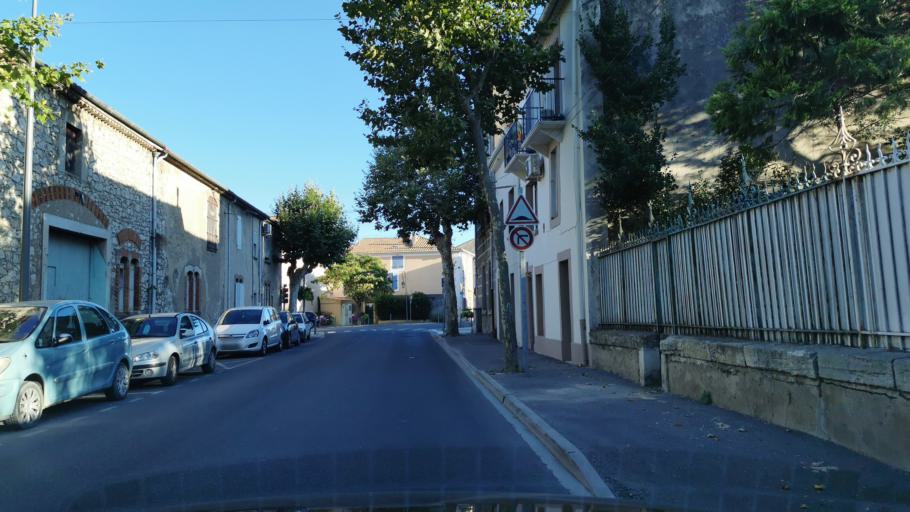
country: FR
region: Languedoc-Roussillon
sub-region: Departement de l'Aude
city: Moussan
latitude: 43.2449
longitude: 2.9975
